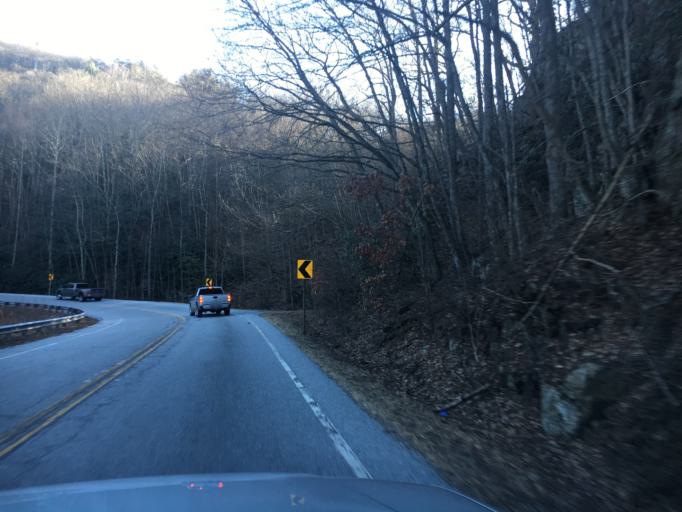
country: US
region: Georgia
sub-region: Union County
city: Blairsville
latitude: 34.7503
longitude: -83.9236
